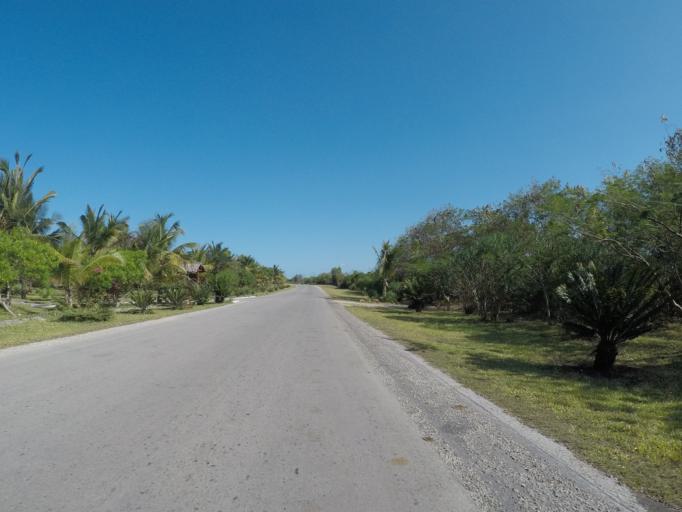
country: TZ
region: Zanzibar Central/South
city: Nganane
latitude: -6.1827
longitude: 39.5280
